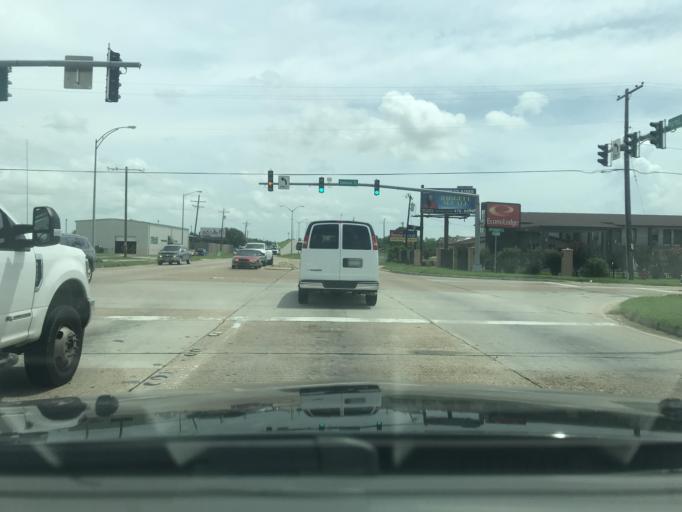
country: US
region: Louisiana
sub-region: Calcasieu Parish
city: Lake Charles
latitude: 30.2425
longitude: -93.1806
